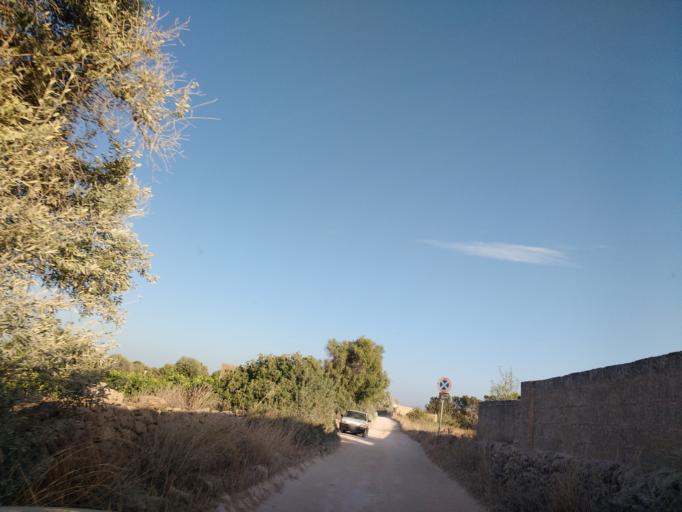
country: IT
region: Sicily
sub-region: Provincia di Siracusa
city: Noto
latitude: 36.8196
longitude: 15.0966
